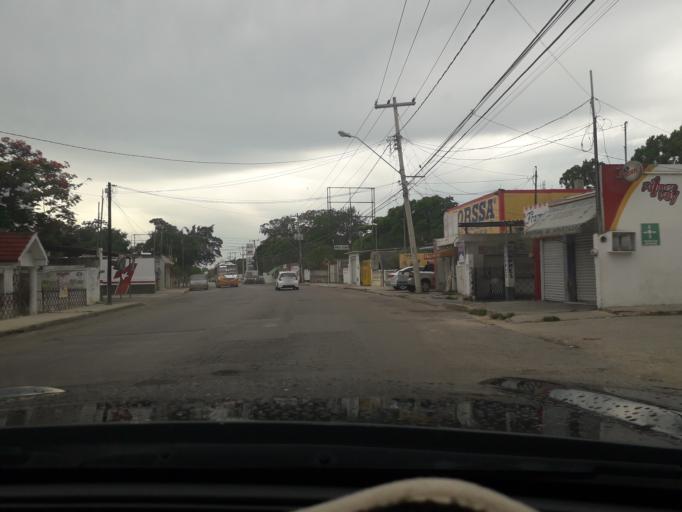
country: MX
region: Yucatan
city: Merida
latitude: 20.9516
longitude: -89.6500
